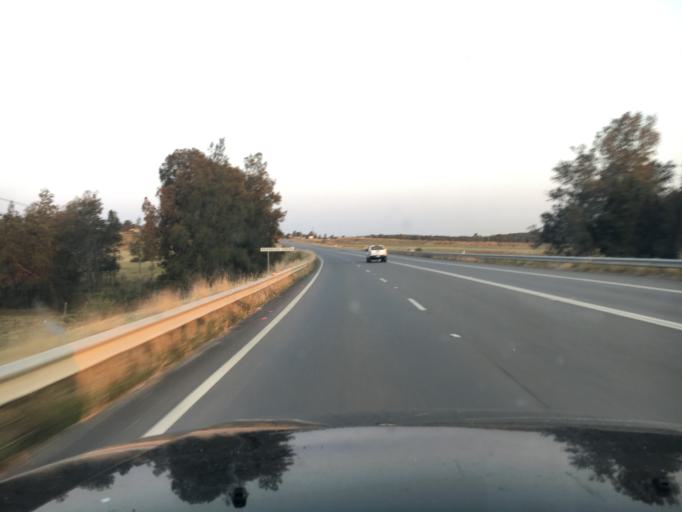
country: AU
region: New South Wales
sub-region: Cessnock
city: Branxton
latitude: -32.6600
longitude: 151.3648
